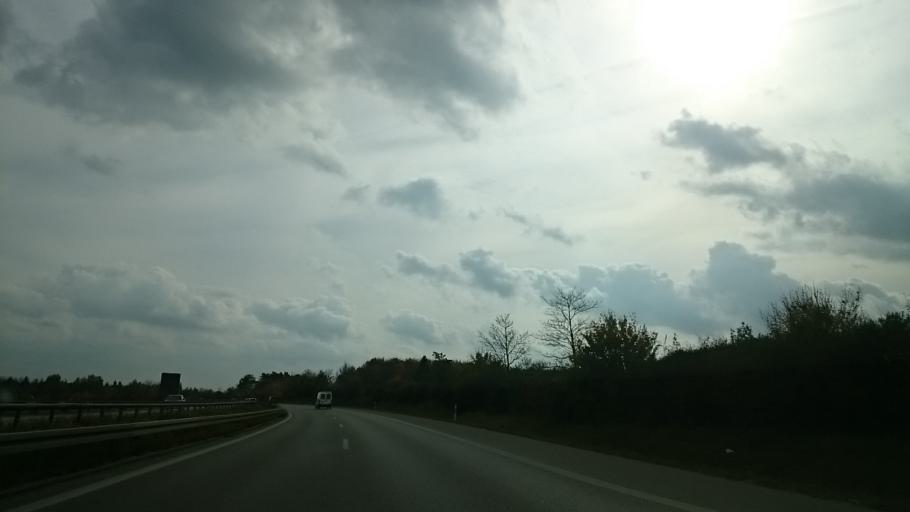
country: DE
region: Bavaria
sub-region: Swabia
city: Langweid
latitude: 48.4818
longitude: 10.8634
